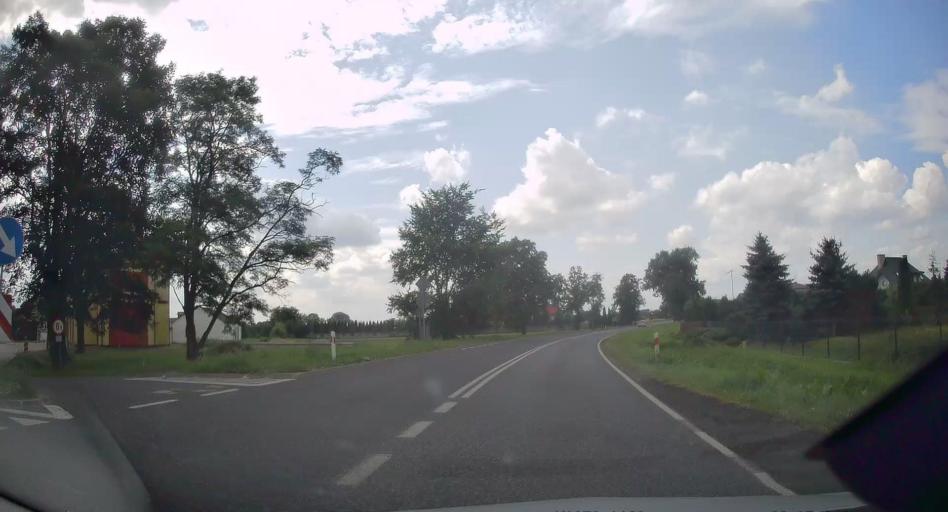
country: PL
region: Lodz Voivodeship
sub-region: Powiat skierniewicki
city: Gluchow
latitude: 51.7792
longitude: 20.0657
